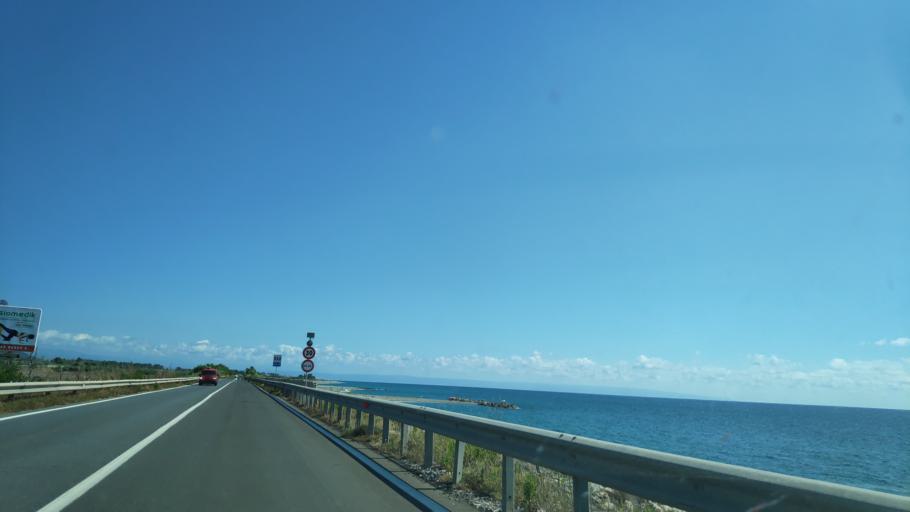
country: IT
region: Calabria
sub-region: Provincia di Cosenza
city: Campora San Giovanni
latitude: 39.0504
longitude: 16.0958
